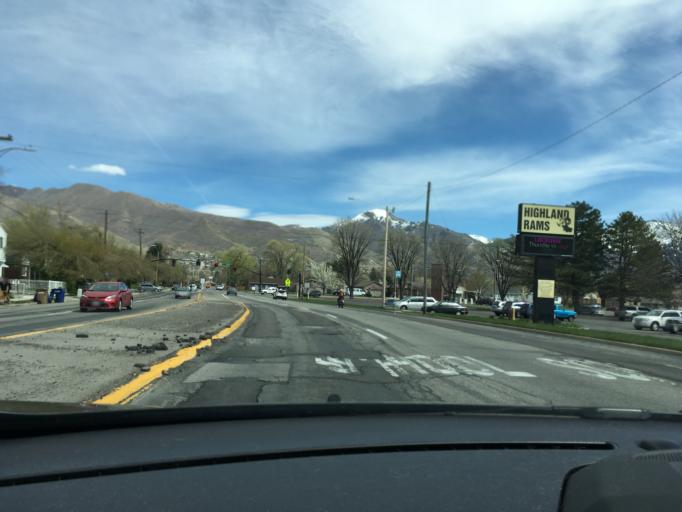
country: US
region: Utah
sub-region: Salt Lake County
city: Willard
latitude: 40.7255
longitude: -111.8439
